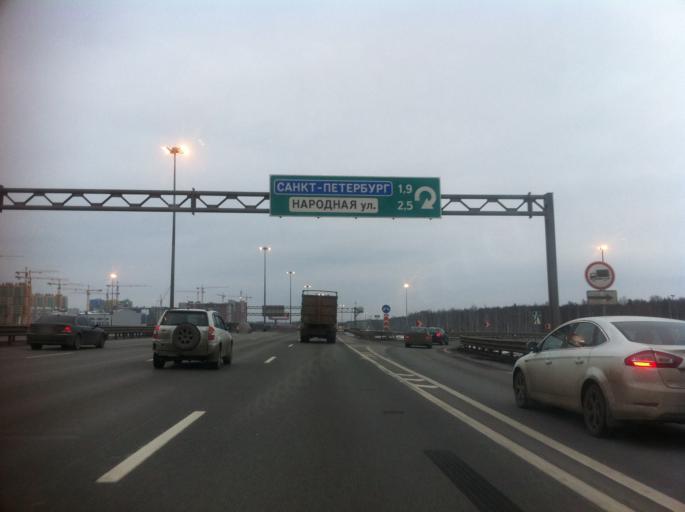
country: RU
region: Leningrad
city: Rybatskoye
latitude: 59.8841
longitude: 30.5265
